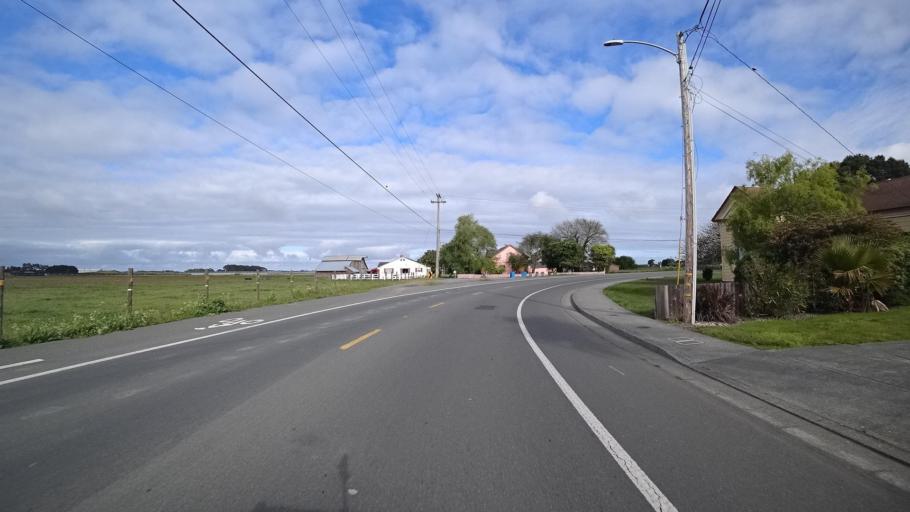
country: US
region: California
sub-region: Humboldt County
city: Arcata
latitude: 40.8929
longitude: -124.0938
